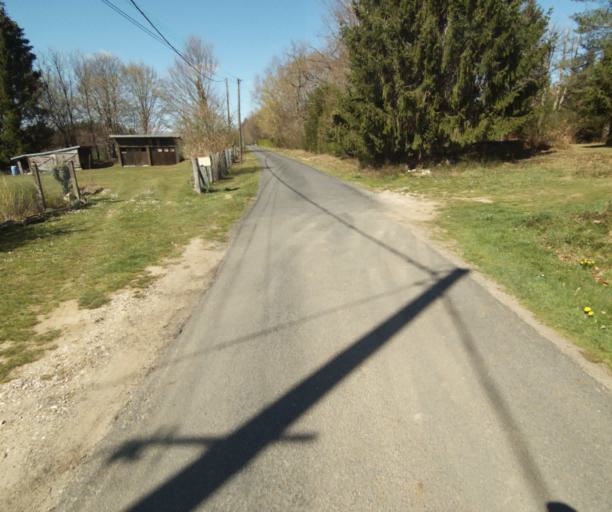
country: FR
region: Limousin
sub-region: Departement de la Correze
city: Saint-Clement
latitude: 45.3115
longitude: 1.6785
